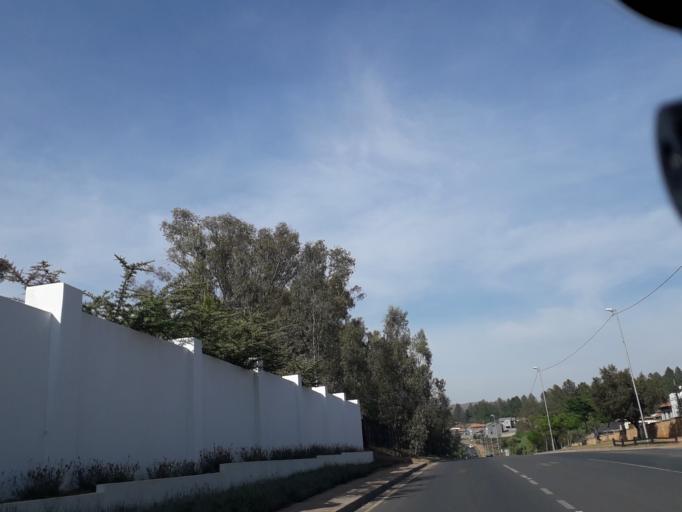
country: ZA
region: Gauteng
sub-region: West Rand District Municipality
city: Muldersdriseloop
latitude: -26.0745
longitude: 27.8851
